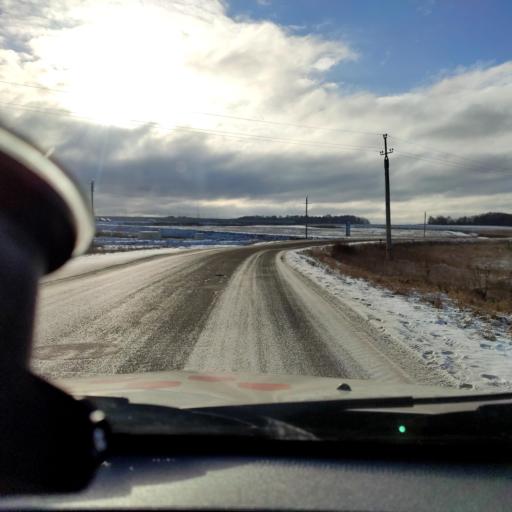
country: RU
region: Bashkortostan
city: Mikhaylovka
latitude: 54.7990
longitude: 55.7800
